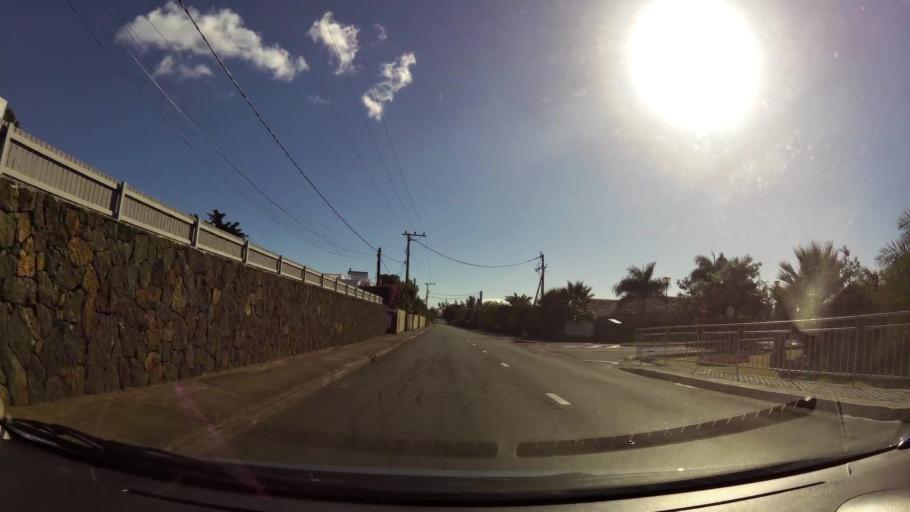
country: MU
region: Black River
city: Tamarin
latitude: -20.3404
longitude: 57.3644
